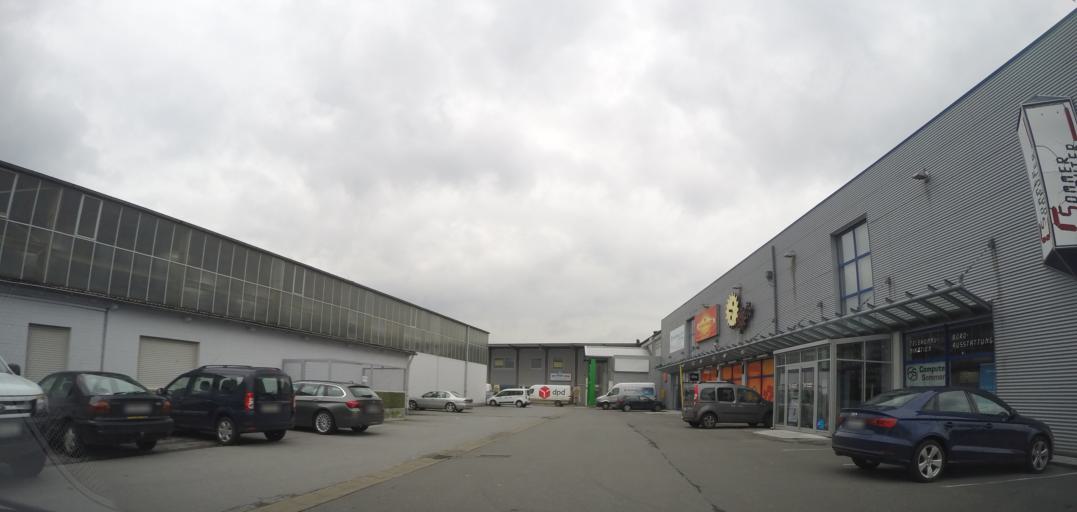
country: DE
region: North Rhine-Westphalia
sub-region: Regierungsbezirk Arnsberg
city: Lippstadt
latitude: 51.6513
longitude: 8.3449
